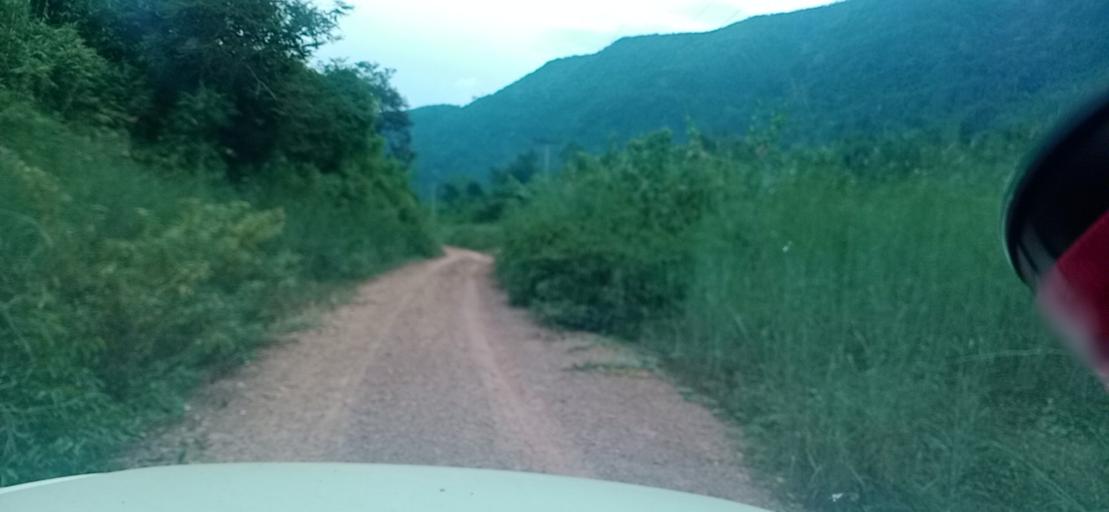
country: TH
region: Changwat Bueng Kan
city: Pak Khat
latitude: 18.5631
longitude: 103.2841
